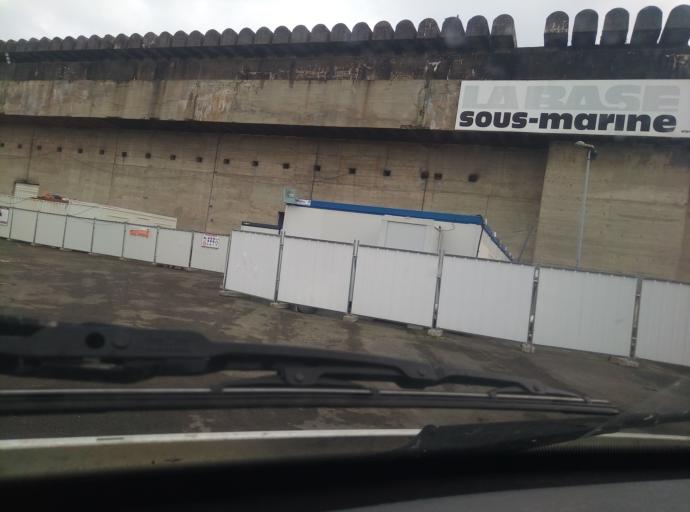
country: FR
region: Aquitaine
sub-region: Departement de la Gironde
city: Le Bouscat
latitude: 44.8705
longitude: -0.5608
